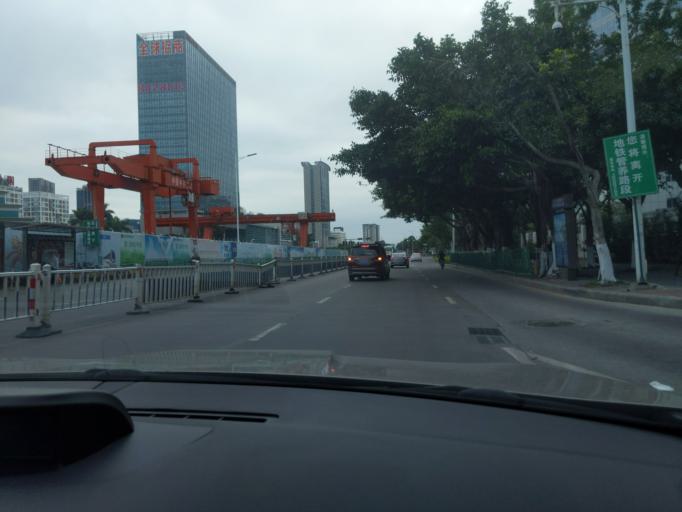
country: CN
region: Fujian
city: Liuwudian
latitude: 24.4855
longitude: 118.1734
